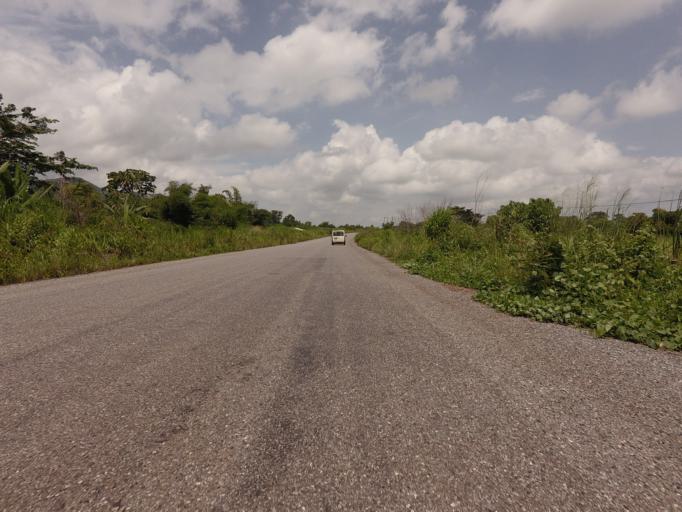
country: GH
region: Volta
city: Kpandu
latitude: 6.8441
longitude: 0.3901
